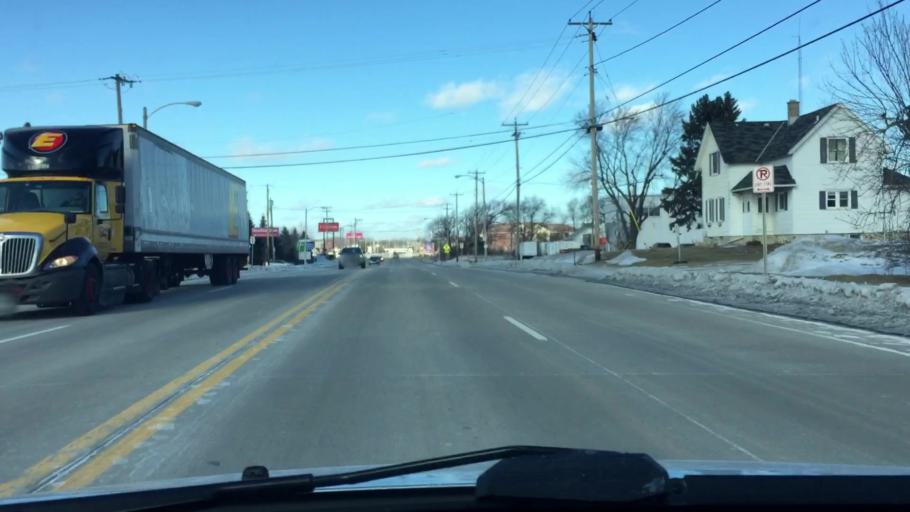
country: US
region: Wisconsin
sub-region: Milwaukee County
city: Greendale
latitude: 42.9241
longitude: -87.9304
